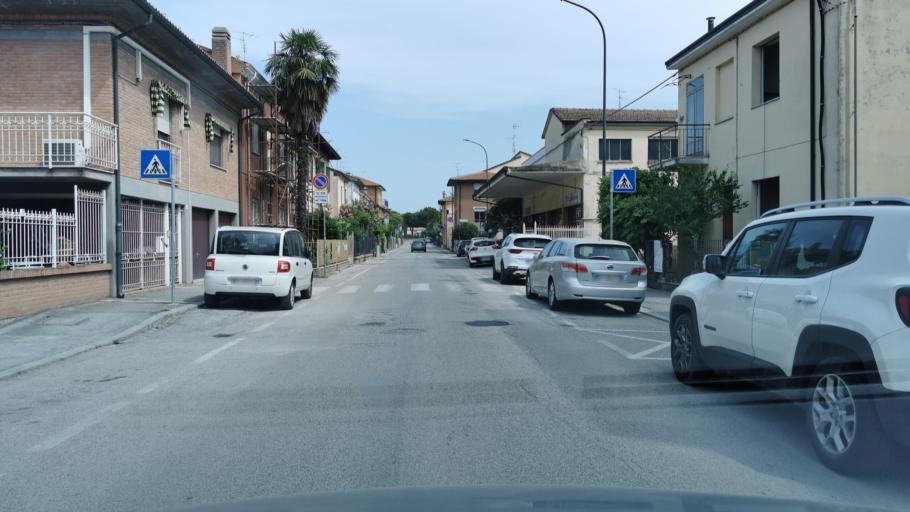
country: IT
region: Emilia-Romagna
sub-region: Provincia di Ravenna
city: Ravenna
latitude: 44.4160
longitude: 12.1853
